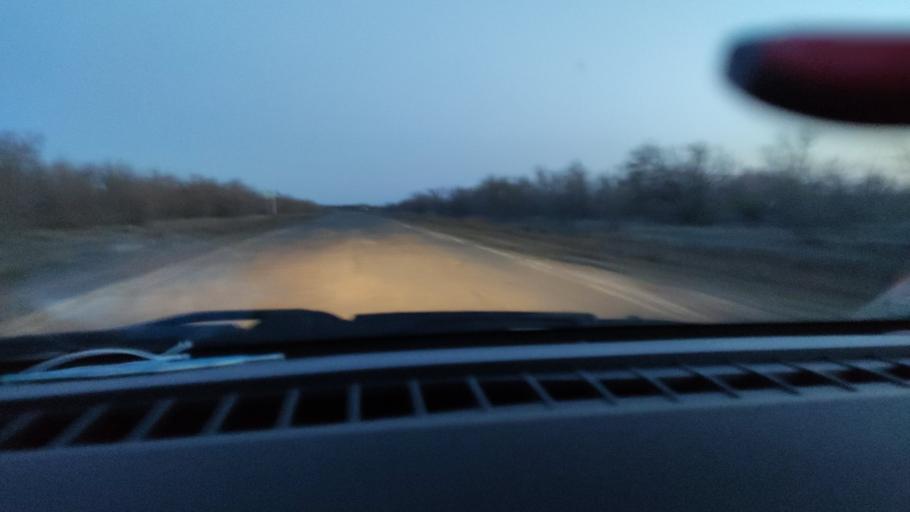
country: RU
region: Saratov
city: Rovnoye
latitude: 50.9695
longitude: 46.1170
